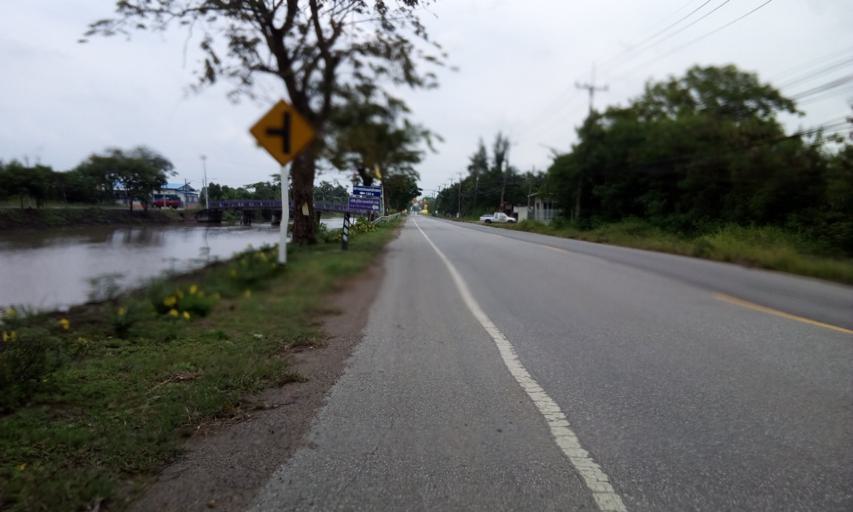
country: TH
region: Pathum Thani
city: Nong Suea
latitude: 14.1075
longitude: 100.8241
